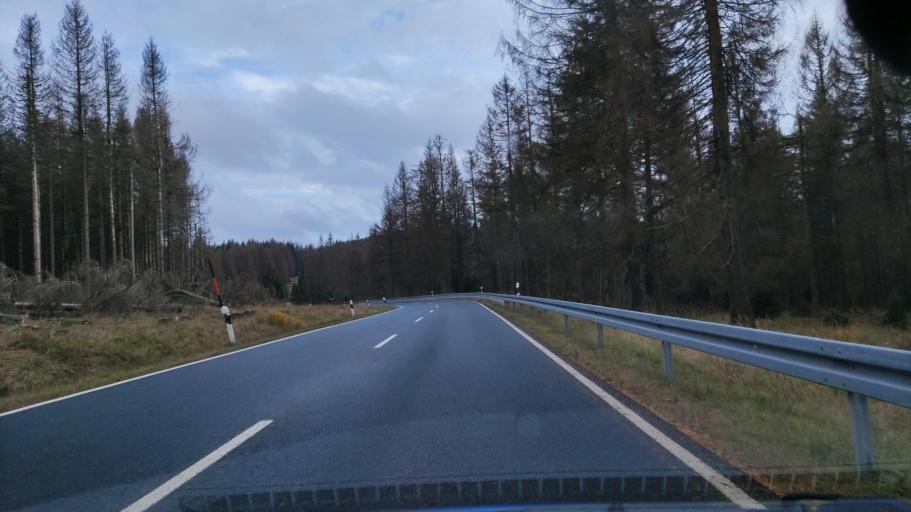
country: DE
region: Lower Saxony
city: Sankt Andreasberg
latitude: 51.7667
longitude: 10.4961
